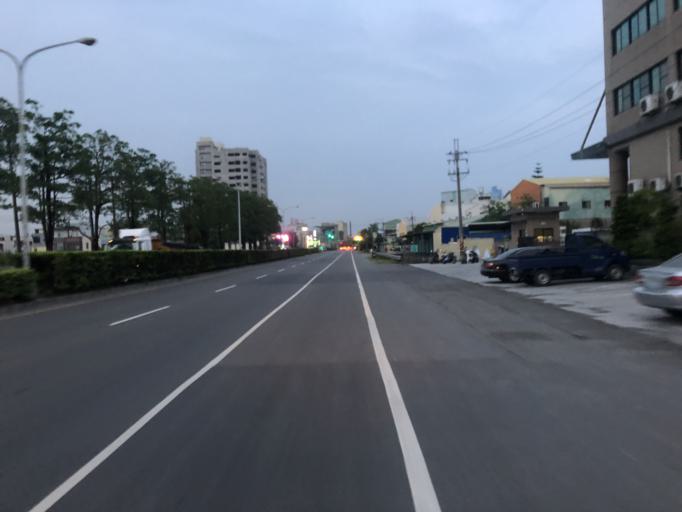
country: TW
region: Taiwan
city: Yujing
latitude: 23.1219
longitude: 120.3187
